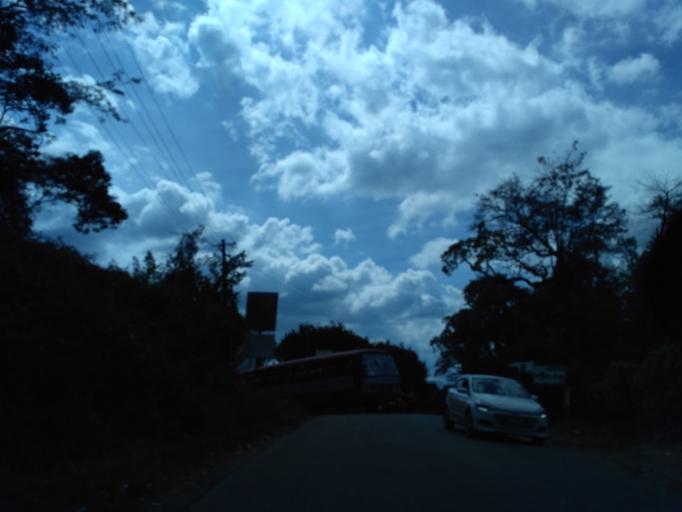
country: IN
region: Karnataka
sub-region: Kodagu
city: Madikeri
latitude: 12.3585
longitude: 75.6960
